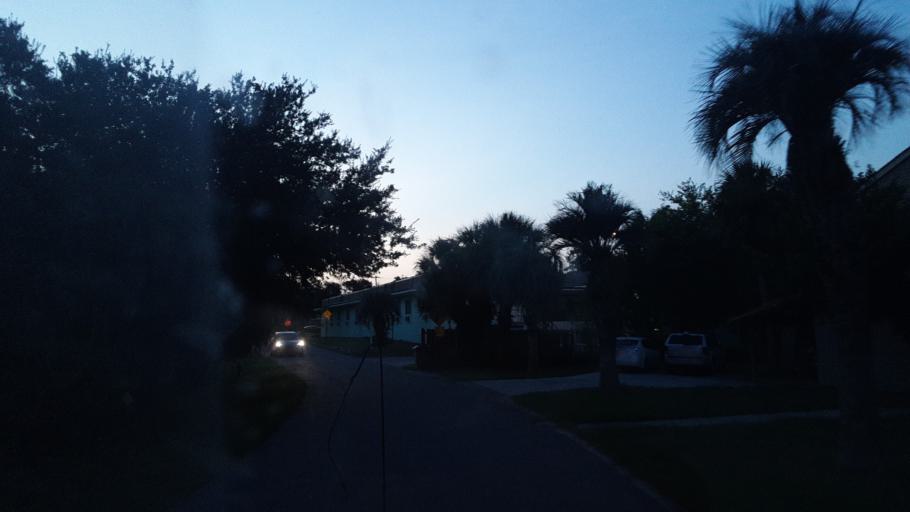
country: US
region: Georgia
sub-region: Chatham County
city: Tybee Island
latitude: 32.0167
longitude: -80.8452
